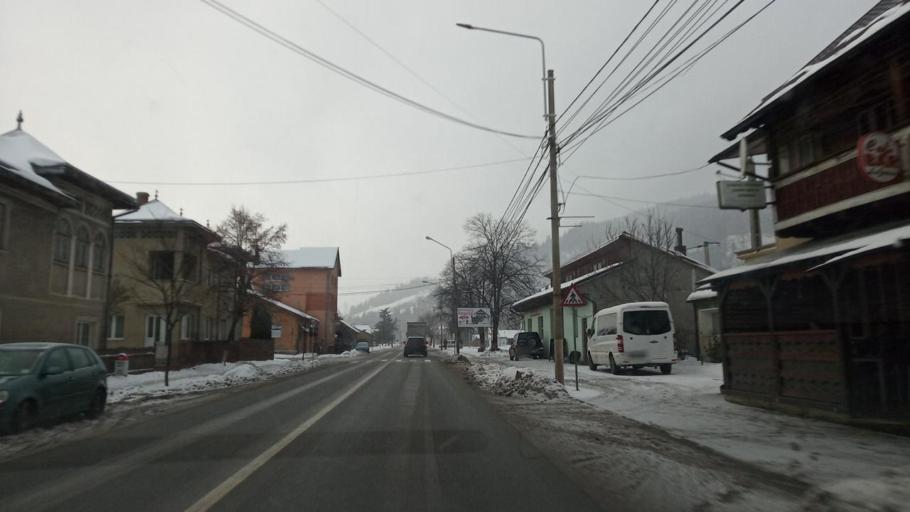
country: RO
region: Suceava
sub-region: Municipiul Vatra Dornei
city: Vatra Dornei
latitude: 47.3476
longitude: 25.3406
